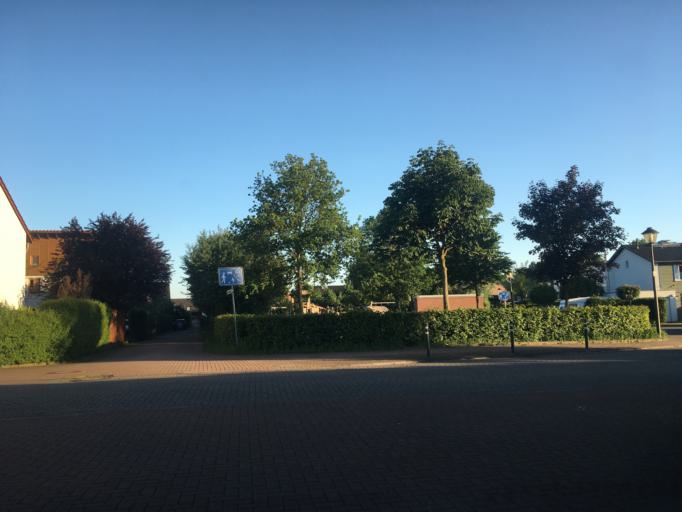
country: DE
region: North Rhine-Westphalia
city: Ludinghausen
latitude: 51.7636
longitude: 7.4594
